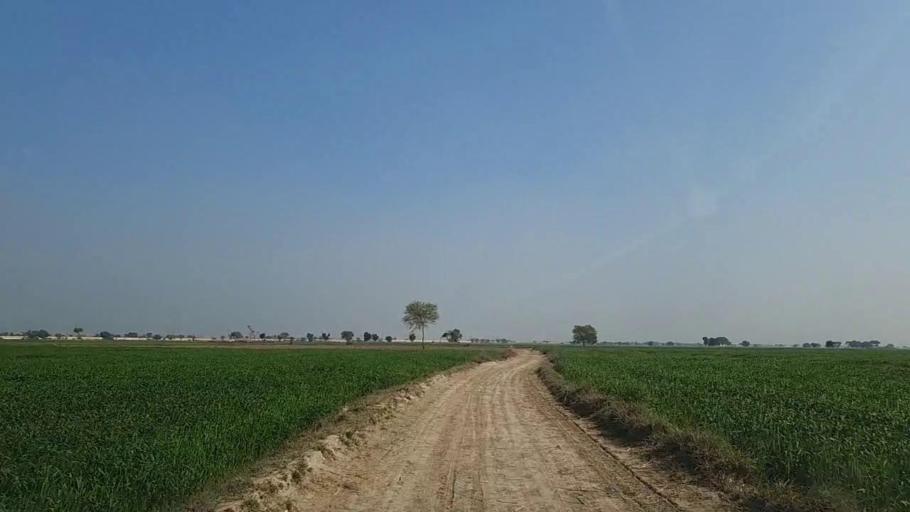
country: PK
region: Sindh
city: Moro
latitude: 26.6812
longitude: 67.9316
